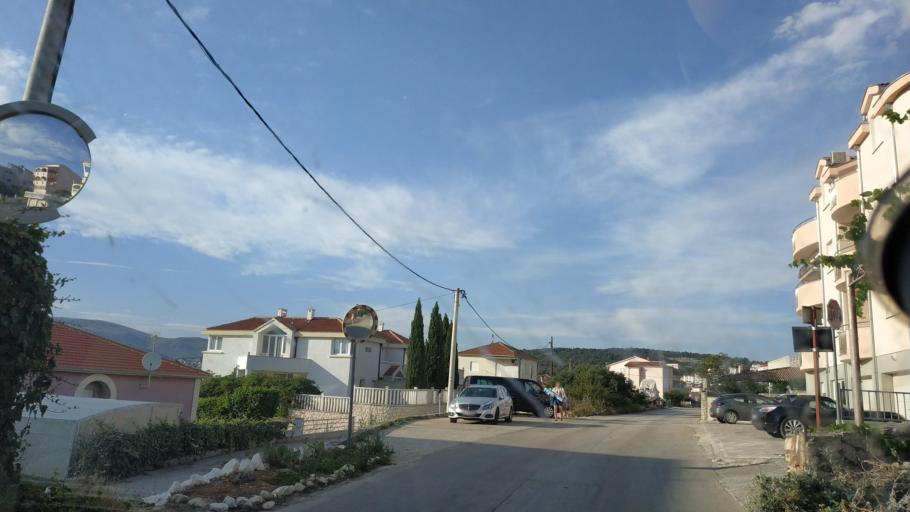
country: HR
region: Splitsko-Dalmatinska
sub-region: Grad Trogir
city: Trogir
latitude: 43.4923
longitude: 16.2574
